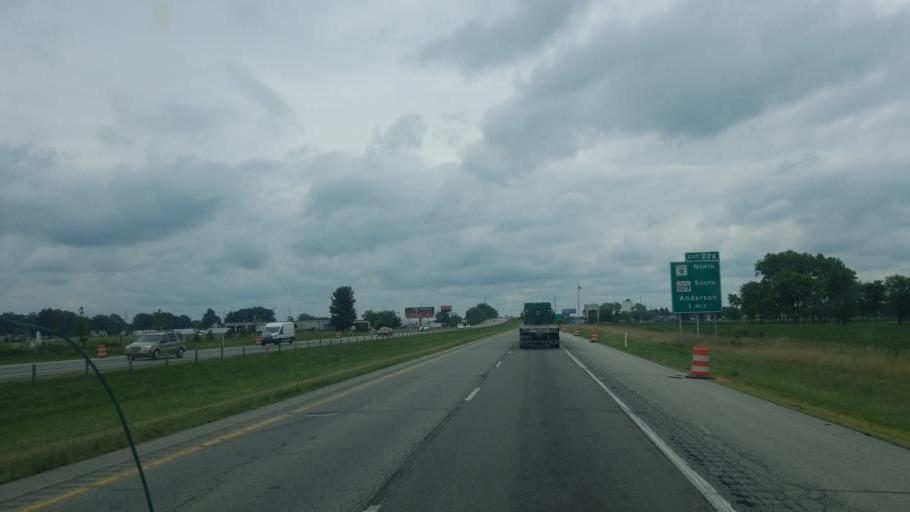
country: US
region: Indiana
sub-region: Madison County
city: Anderson
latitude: 40.0509
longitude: -85.6708
